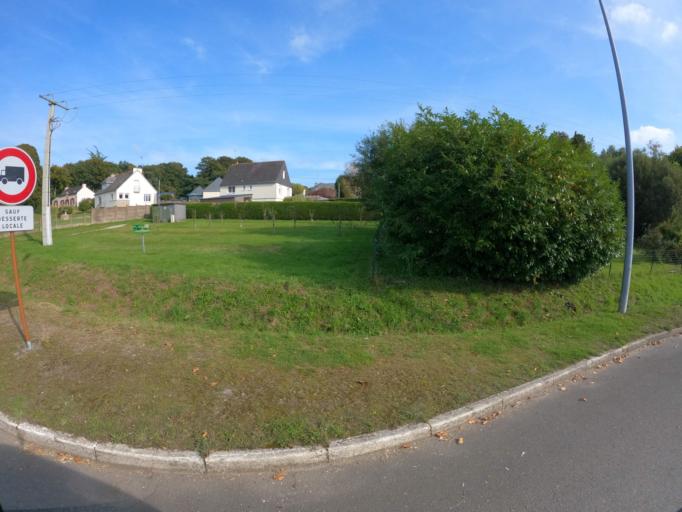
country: FR
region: Brittany
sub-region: Departement du Morbihan
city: Guillac
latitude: 47.8629
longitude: -2.4256
